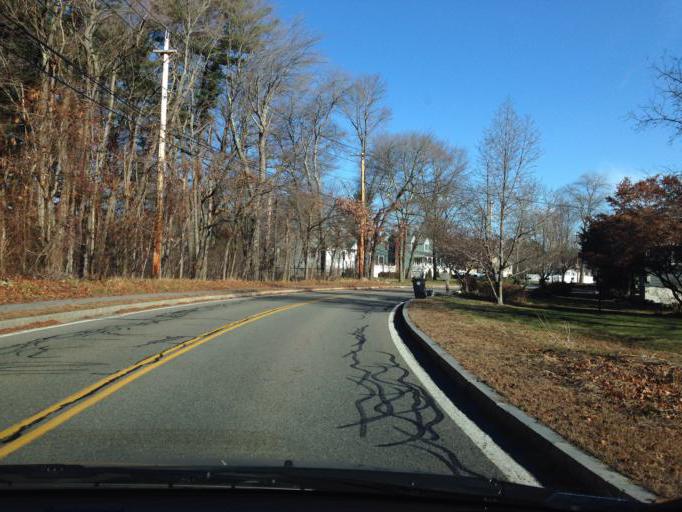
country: US
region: Massachusetts
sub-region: Middlesex County
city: Bedford
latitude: 42.4793
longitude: -71.2850
